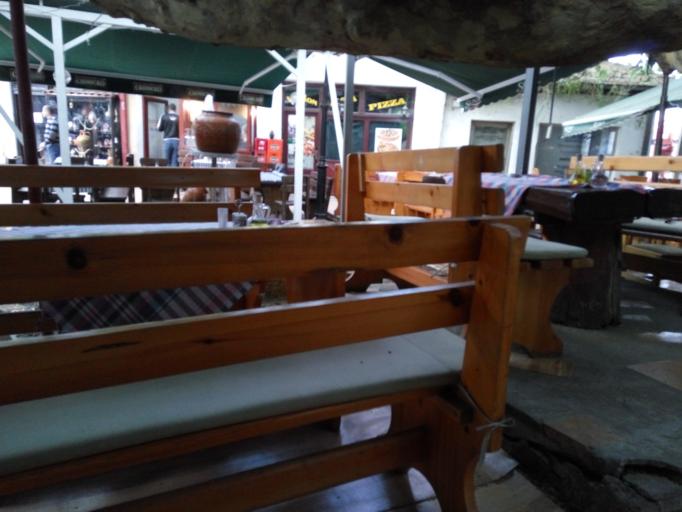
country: MK
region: Karpos
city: Skopje
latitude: 42.0004
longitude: 21.4369
